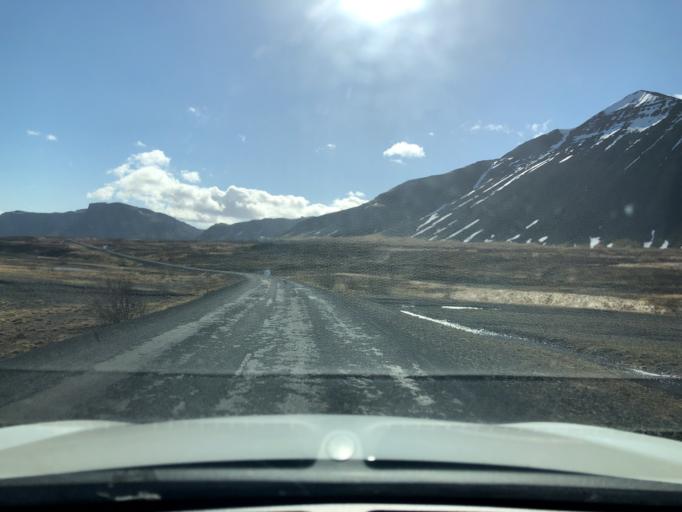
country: IS
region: West
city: Borgarnes
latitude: 64.5244
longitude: -21.8721
